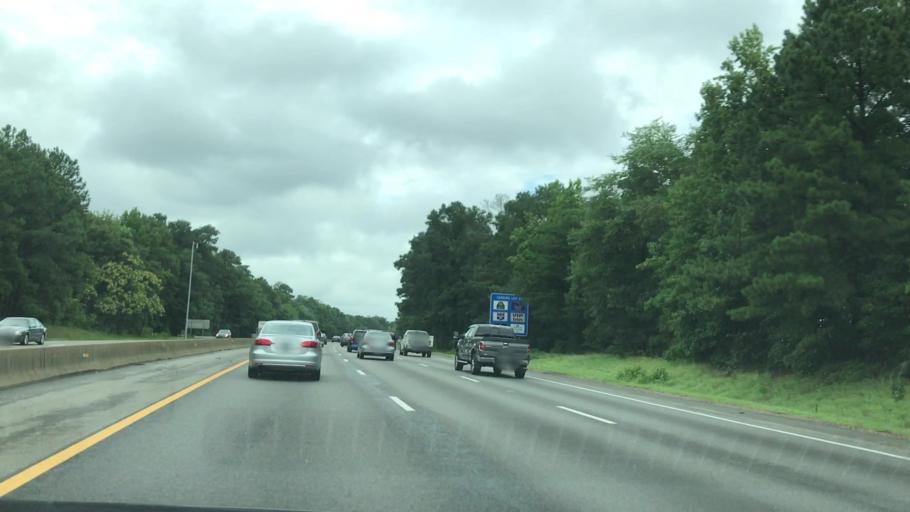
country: US
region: Virginia
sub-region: Chesterfield County
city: Chester
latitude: 37.3859
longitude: -77.4184
